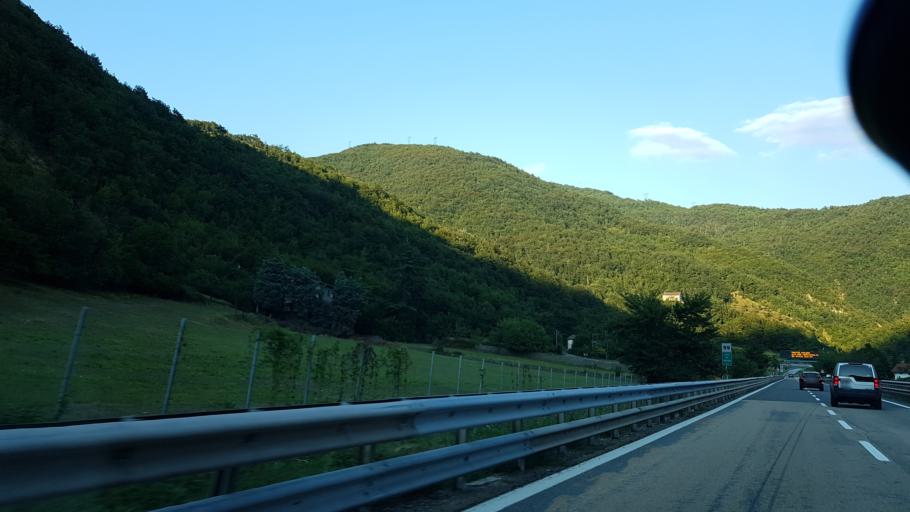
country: IT
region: Liguria
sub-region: Provincia di Genova
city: Isola del Cantone
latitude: 44.6510
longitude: 8.9518
